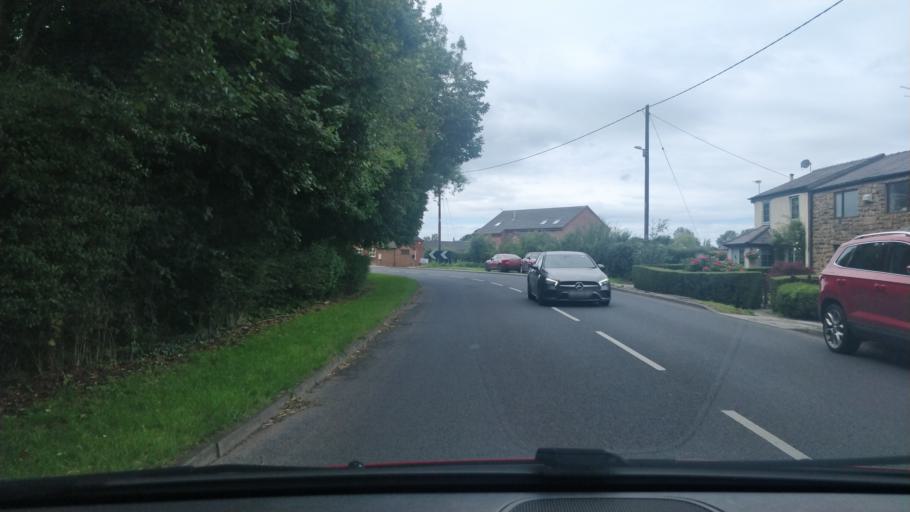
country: GB
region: England
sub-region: Lancashire
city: Leyland
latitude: 53.7027
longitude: -2.7373
